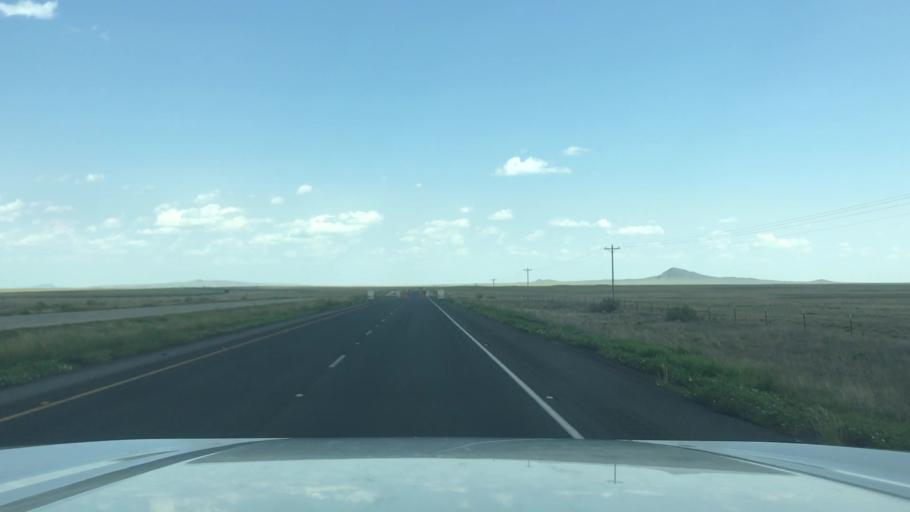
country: US
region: New Mexico
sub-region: Union County
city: Clayton
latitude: 36.6224
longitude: -103.6987
